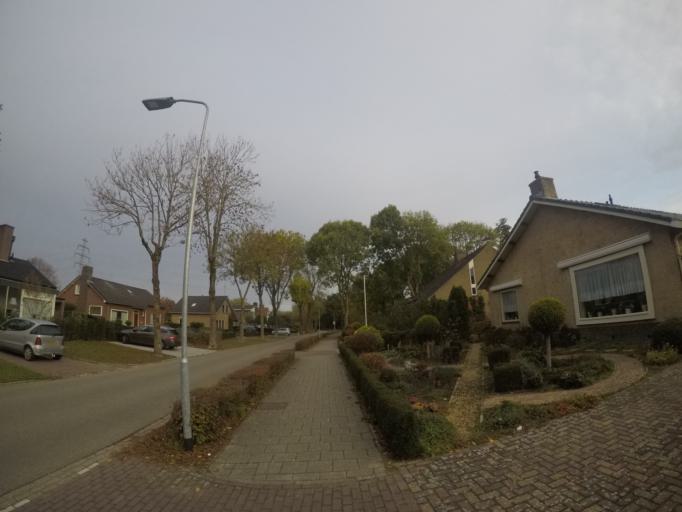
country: NL
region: Gelderland
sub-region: Gemeente Zevenaar
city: Zevenaar
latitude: 51.9166
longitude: 6.0805
